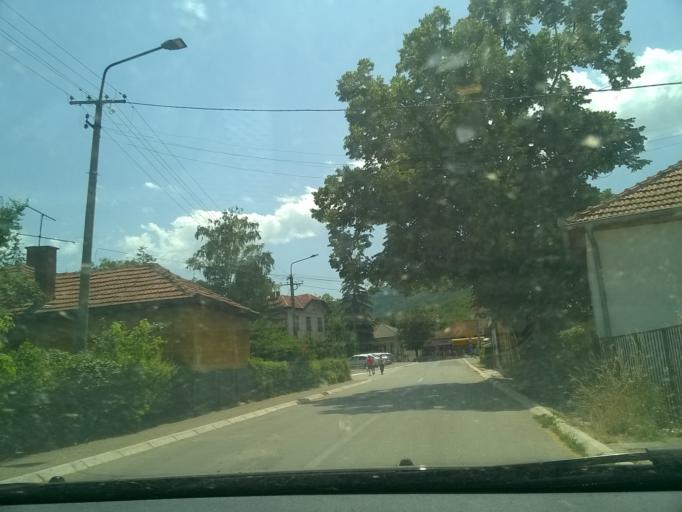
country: RS
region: Central Serbia
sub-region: Zajecarski Okrug
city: Soko Banja
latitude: 43.6450
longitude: 21.8760
